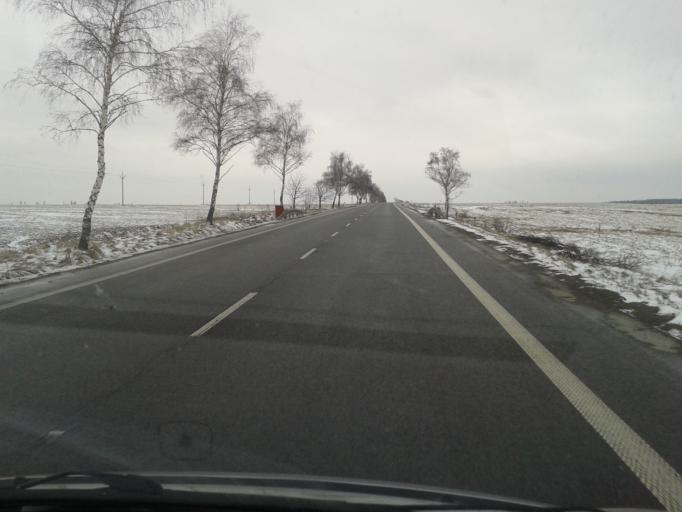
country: SK
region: Zilinsky
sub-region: Okres Zilina
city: Trstena
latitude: 49.3849
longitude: 19.6363
